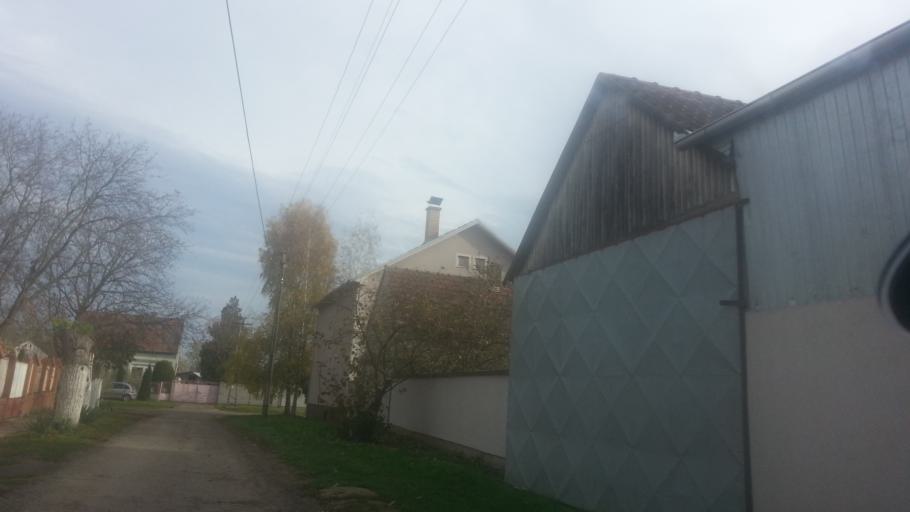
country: RS
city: Putinci
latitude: 44.9959
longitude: 19.9698
